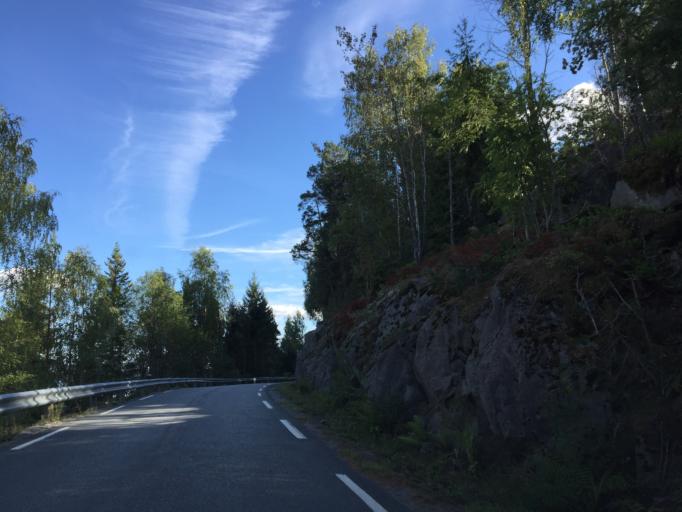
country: NO
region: Buskerud
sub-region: Ovre Eiker
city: Hokksund
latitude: 59.6544
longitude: 9.9129
